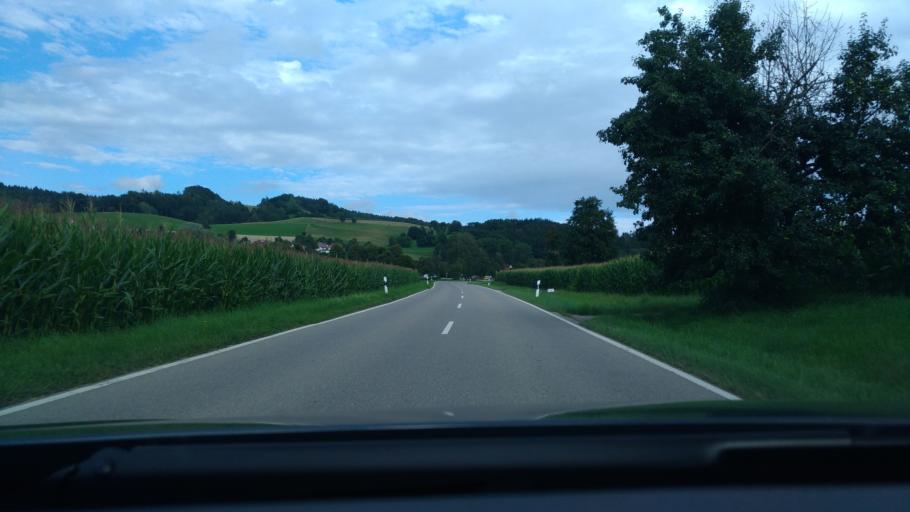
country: DE
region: Baden-Wuerttemberg
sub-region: Tuebingen Region
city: Sipplingen
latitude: 47.8266
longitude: 9.0890
